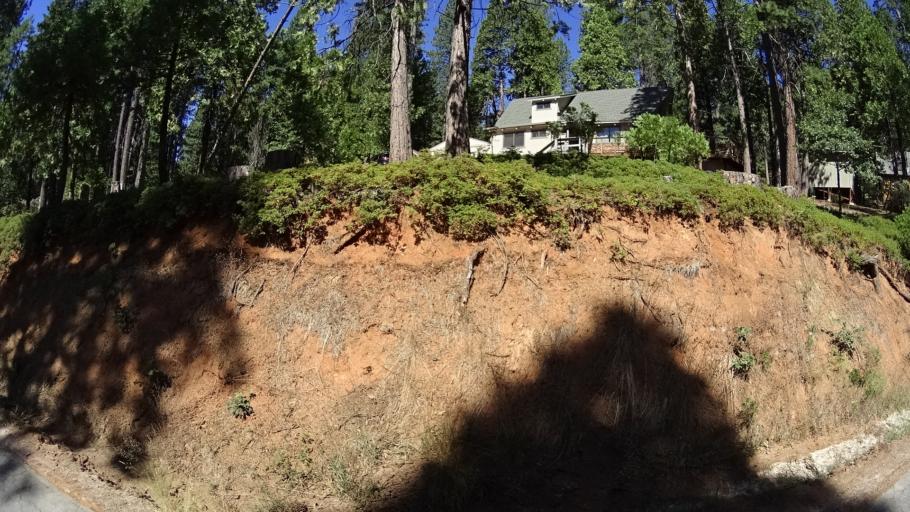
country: US
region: California
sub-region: Calaveras County
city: Arnold
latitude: 38.2491
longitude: -120.3396
